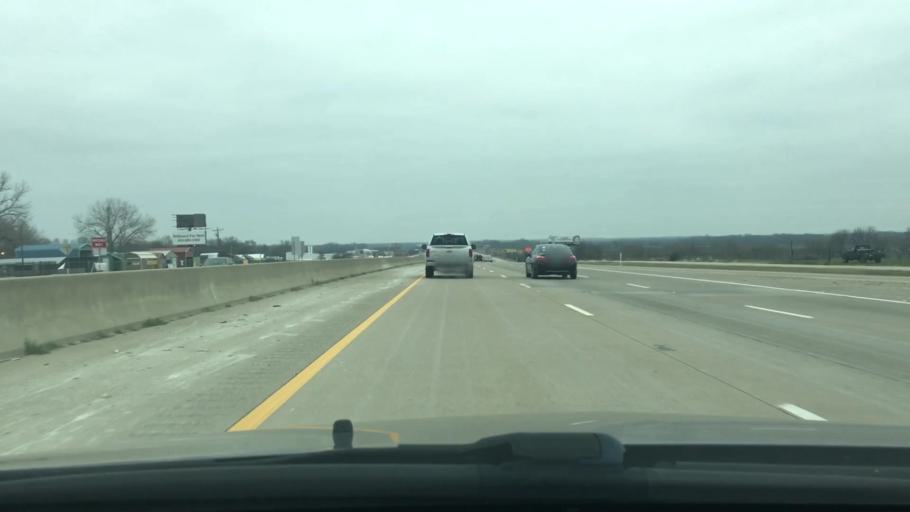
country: US
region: Texas
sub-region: Navarro County
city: Corsicana
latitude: 32.1969
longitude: -96.4735
